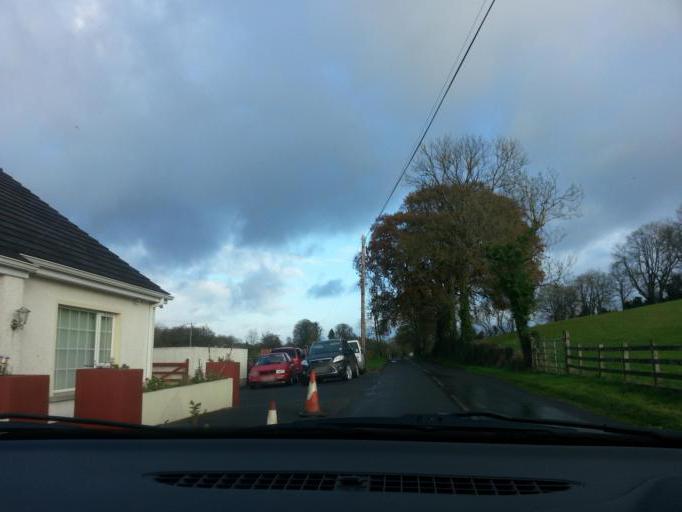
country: IE
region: Ulster
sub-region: County Monaghan
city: Clones
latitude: 54.1947
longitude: -7.2945
